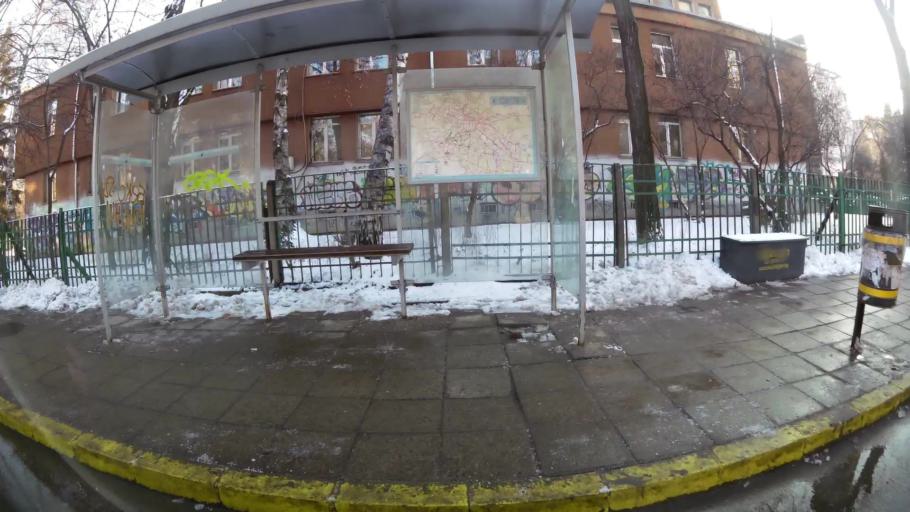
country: BG
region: Sofia-Capital
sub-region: Stolichna Obshtina
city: Sofia
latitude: 42.6831
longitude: 23.3624
